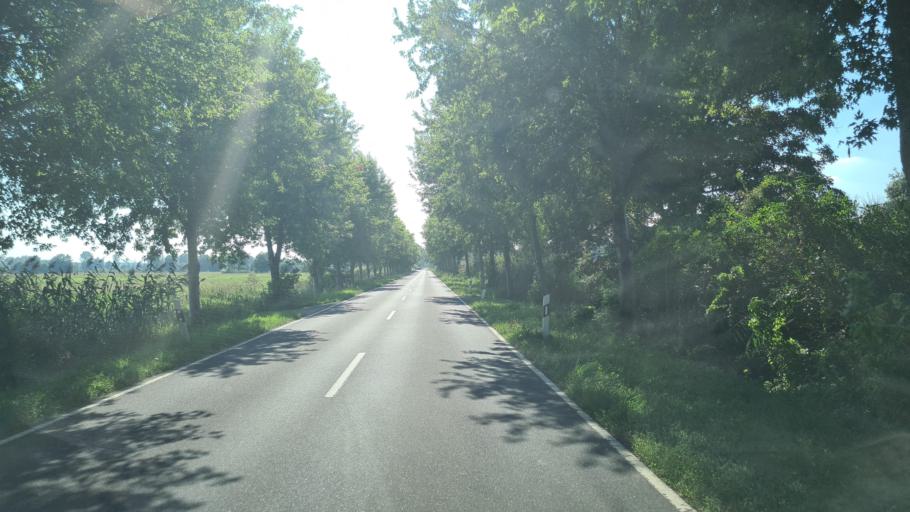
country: DE
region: Brandenburg
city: Friesack
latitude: 52.7660
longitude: 12.5907
